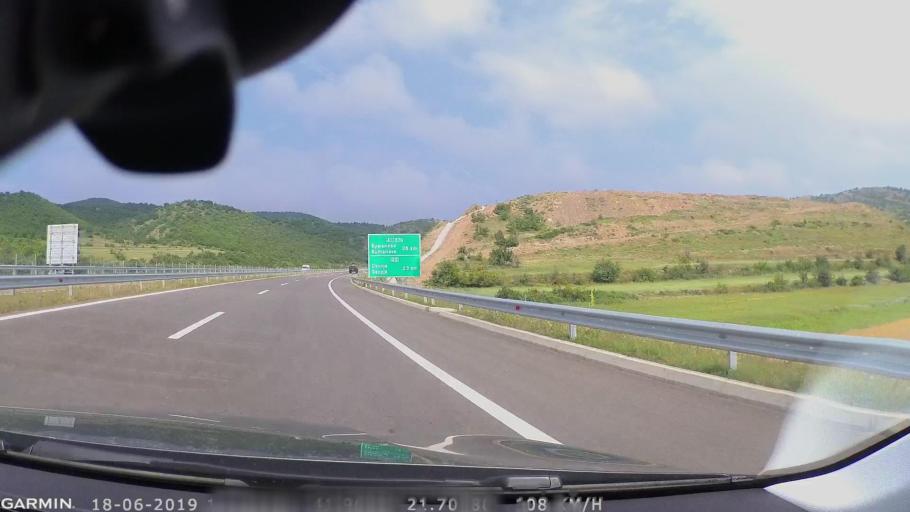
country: MK
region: Petrovec
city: Sredno Konjare
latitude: 41.9474
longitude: 21.7995
